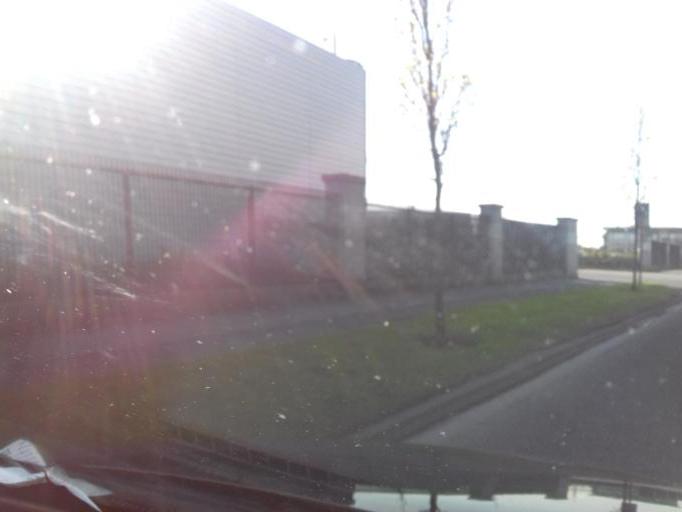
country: IE
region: Leinster
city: Castleknock
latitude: 53.4033
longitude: -6.3388
